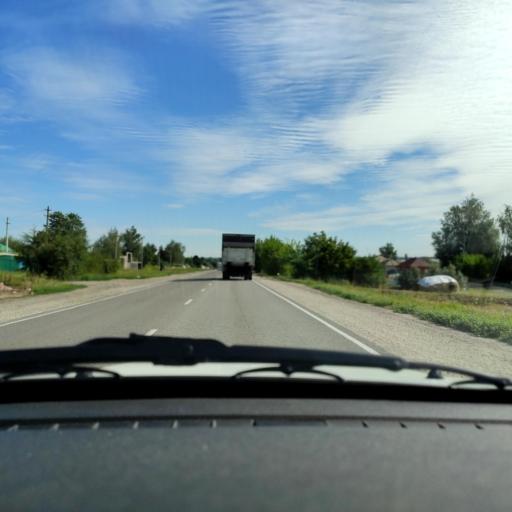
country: RU
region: Voronezj
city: Orlovo
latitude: 51.7450
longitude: 39.5791
